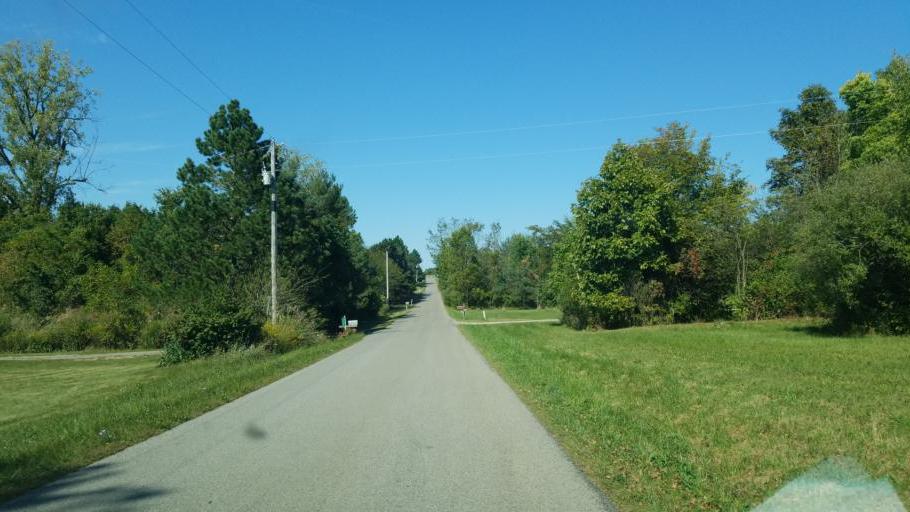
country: US
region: Ohio
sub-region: Logan County
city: Bellefontaine
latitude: 40.3110
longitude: -83.7159
